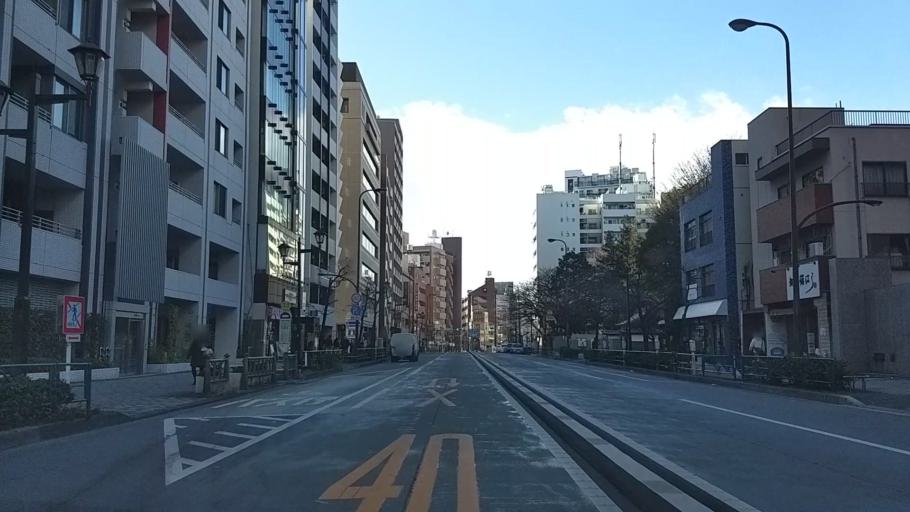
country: JP
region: Tokyo
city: Tokyo
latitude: 35.7329
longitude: 139.7026
